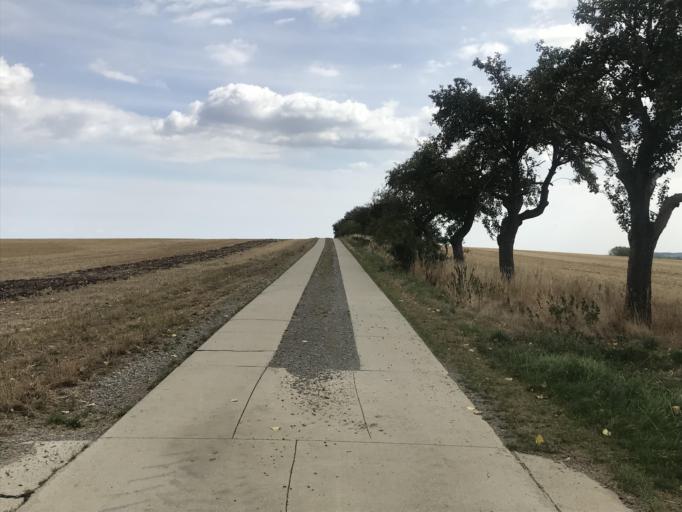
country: DE
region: Saxony-Anhalt
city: Huy-Neinstedt
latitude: 52.0185
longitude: 10.9528
